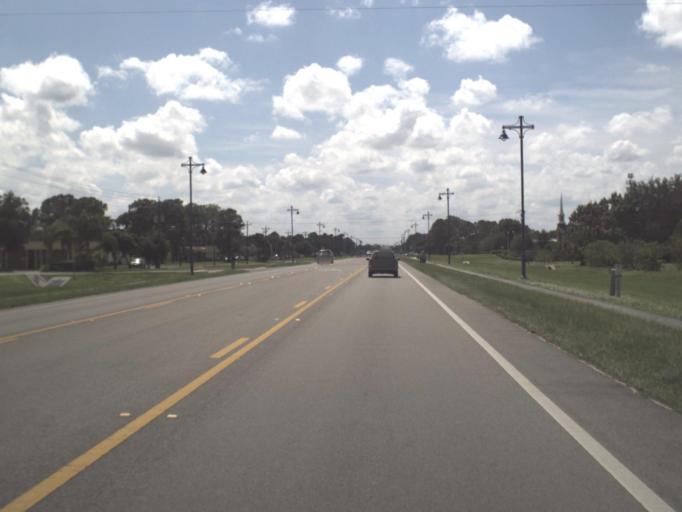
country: US
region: Florida
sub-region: Collier County
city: Immokalee
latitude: 26.4394
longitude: -81.4340
